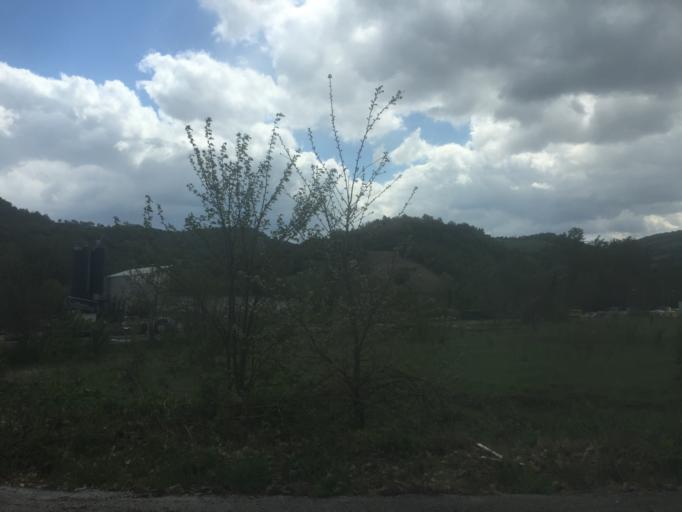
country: IT
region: The Marches
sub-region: Provincia di Macerata
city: Pieve Torina
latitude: 43.0514
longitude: 13.0555
